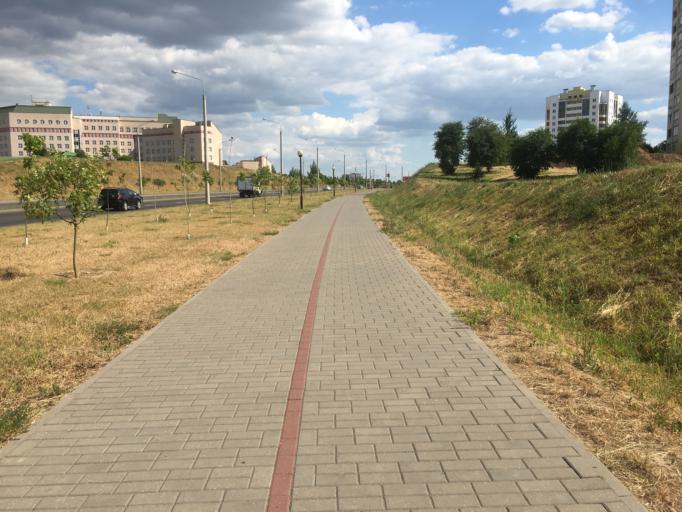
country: BY
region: Grodnenskaya
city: Hrodna
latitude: 53.6832
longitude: 23.8612
